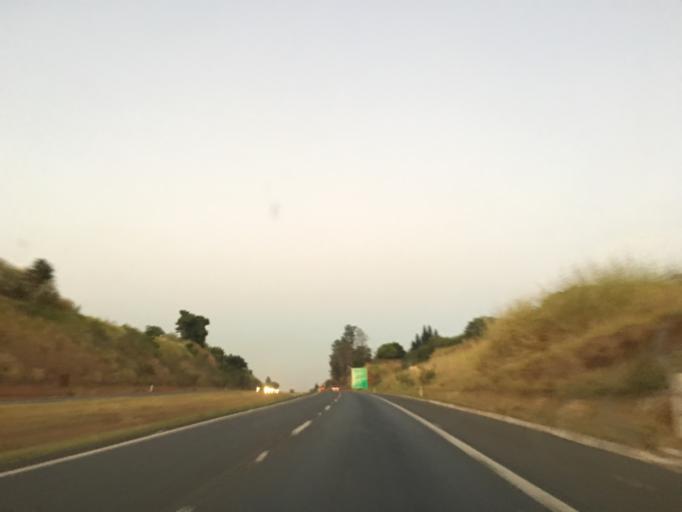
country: BR
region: Sao Paulo
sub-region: Piracicaba
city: Piracicaba
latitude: -22.7205
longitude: -47.6173
